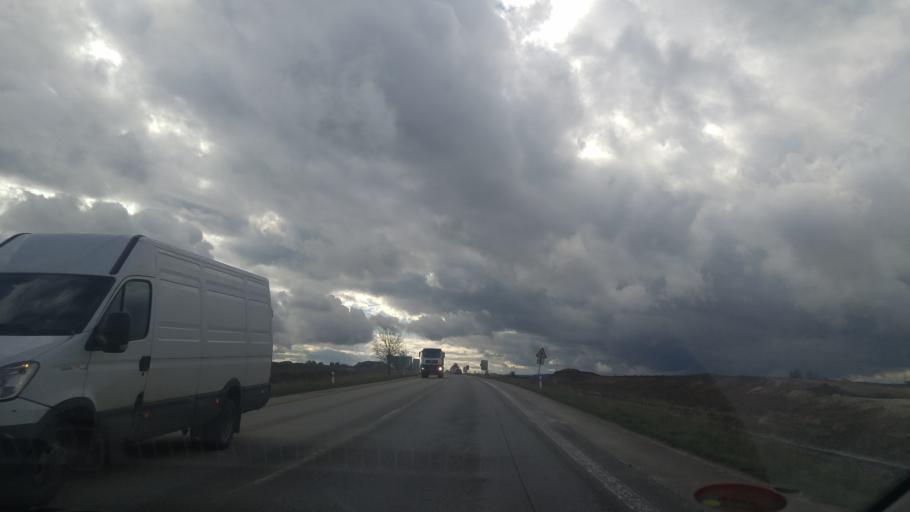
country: CZ
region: Jihocesky
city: Dolni Bukovsko
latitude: 49.1567
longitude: 14.6377
